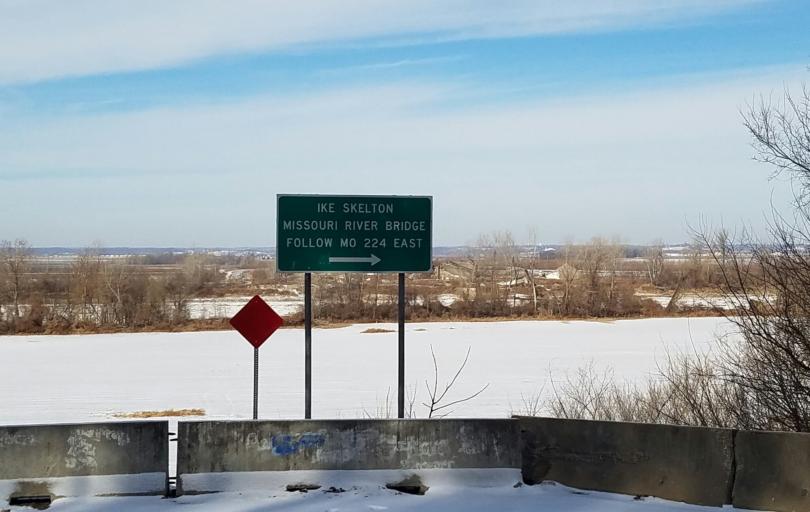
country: US
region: Missouri
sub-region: Lafayette County
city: Lexington
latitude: 39.1834
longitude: -93.8914
